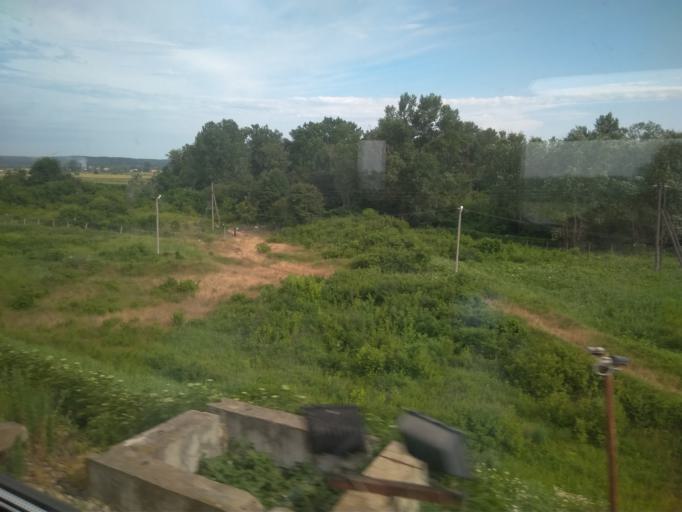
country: RU
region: Krasnodarskiy
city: Pshekhskaya
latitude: 44.7159
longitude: 39.8042
